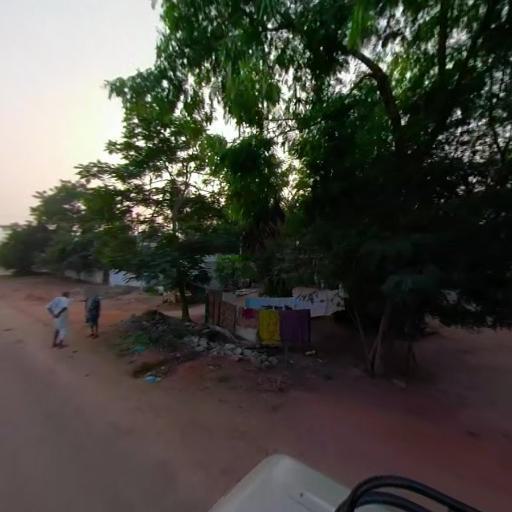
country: IN
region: Telangana
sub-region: Nalgonda
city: Suriapet
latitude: 17.0593
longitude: 79.5474
